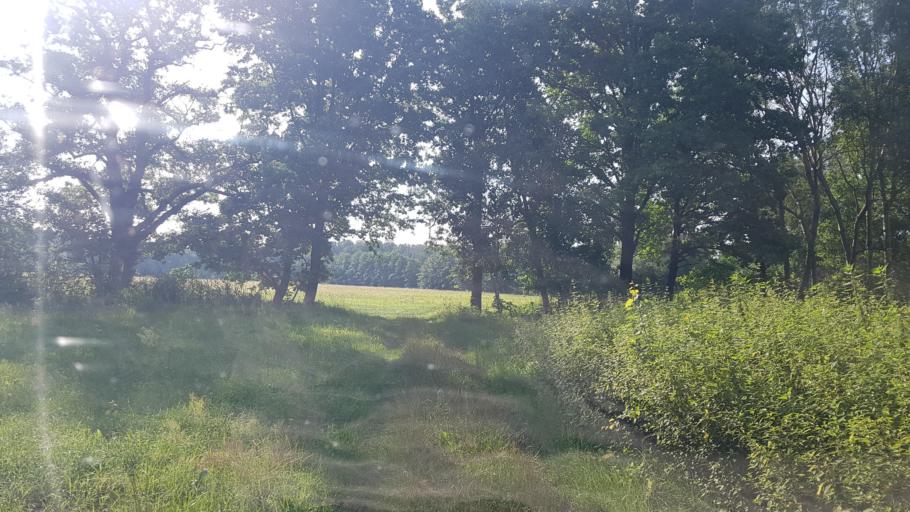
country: DE
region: Brandenburg
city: Finsterwalde
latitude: 51.6745
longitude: 13.7344
